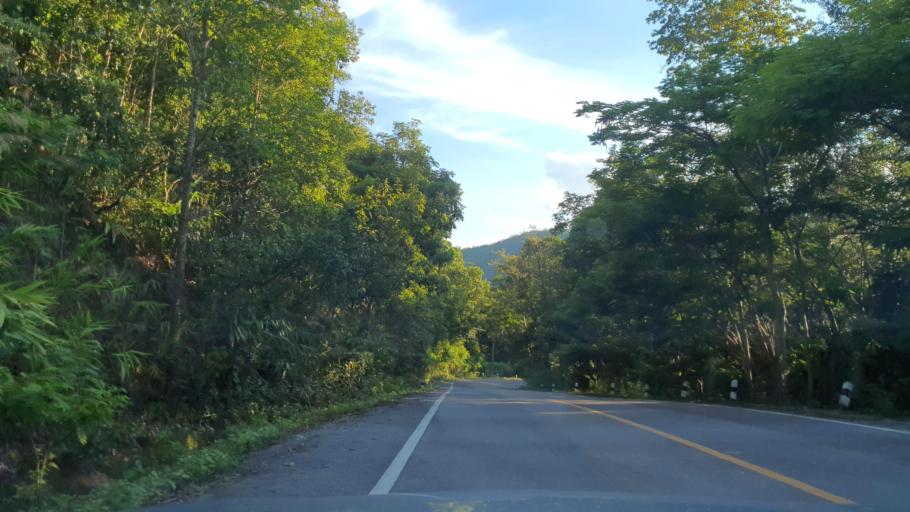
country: TH
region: Chiang Mai
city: Mae On
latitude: 18.8101
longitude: 99.3012
